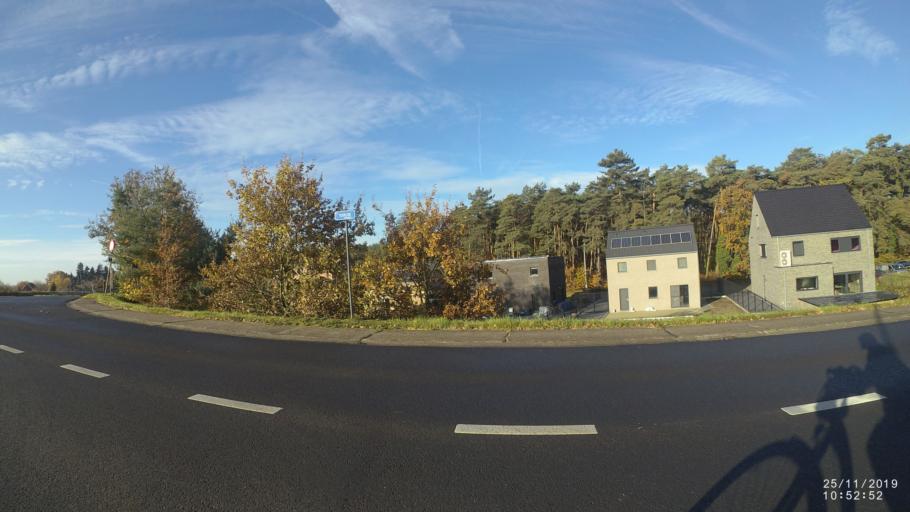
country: BE
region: Flanders
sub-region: Provincie Vlaams-Brabant
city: Scherpenheuvel-Zichem
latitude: 51.0110
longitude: 4.9201
